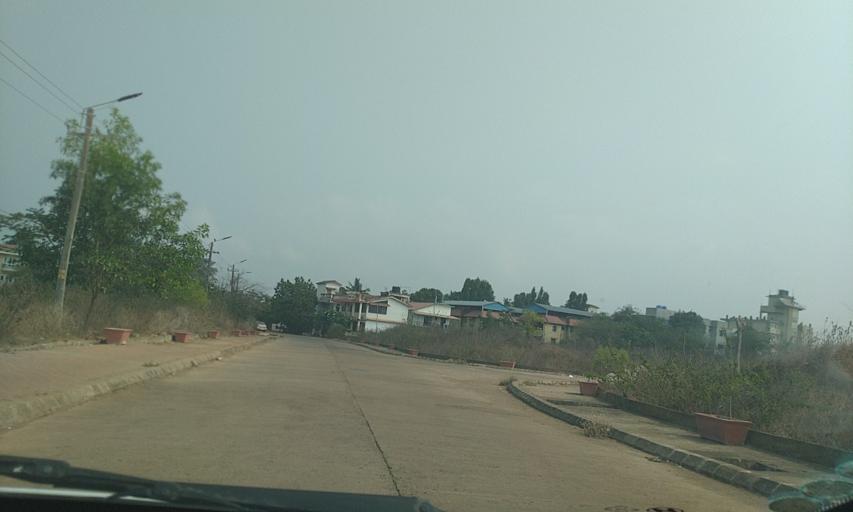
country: IN
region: Goa
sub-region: North Goa
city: Taleigao
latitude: 15.4612
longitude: 73.8174
